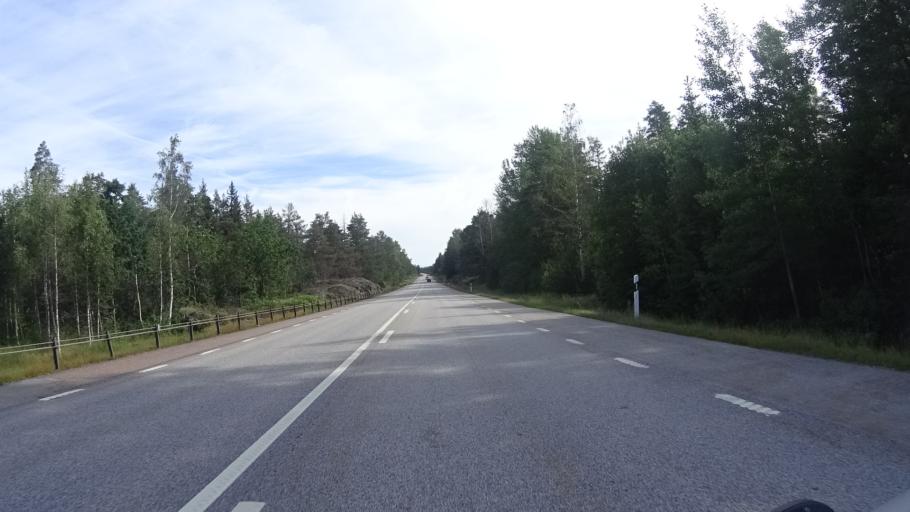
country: SE
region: Kalmar
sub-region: Oskarshamns Kommun
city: Oskarshamn
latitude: 57.4479
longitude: 16.5032
